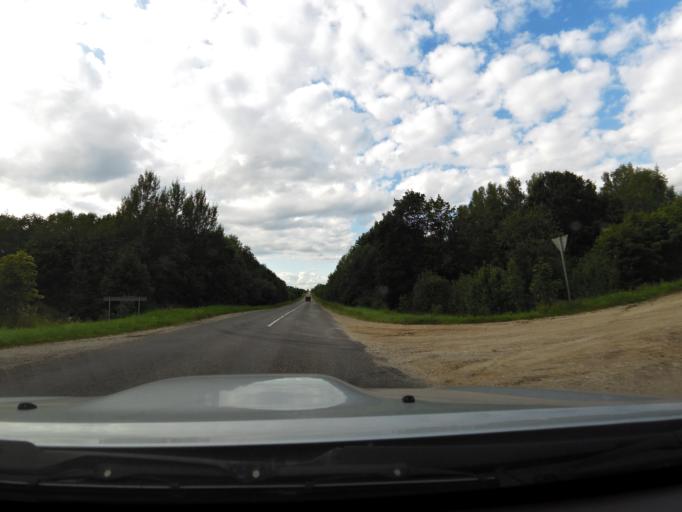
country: LV
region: Akniste
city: Akniste
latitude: 56.0157
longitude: 25.9259
